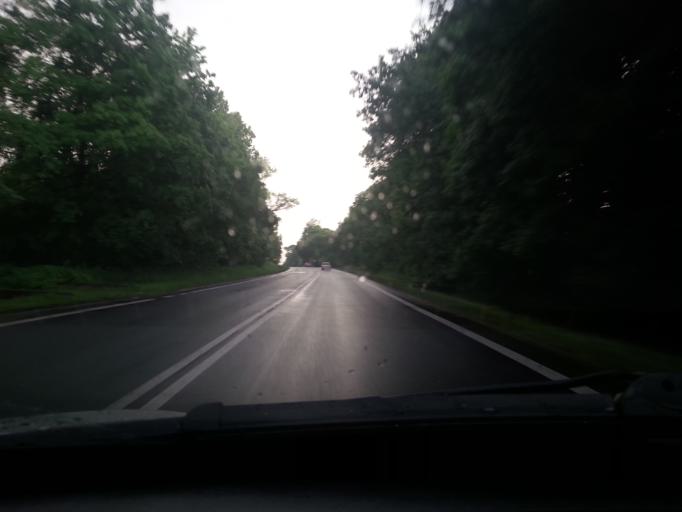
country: PL
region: Lodz Voivodeship
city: Lodz
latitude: 51.8066
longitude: 19.4991
